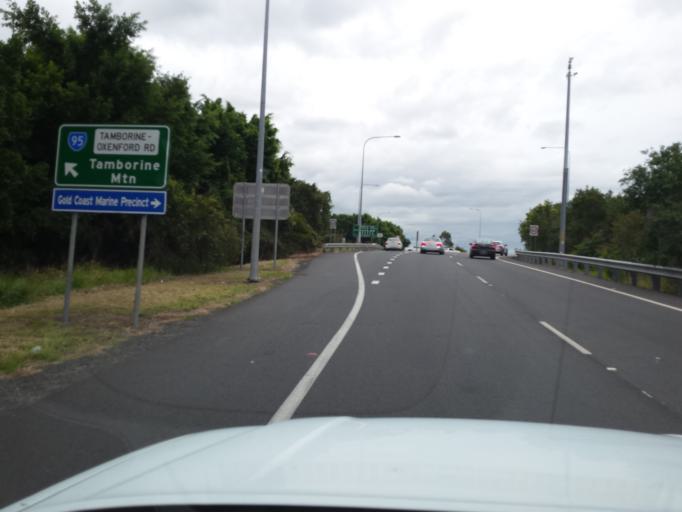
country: AU
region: Queensland
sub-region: Gold Coast
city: Oxenford
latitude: -27.8866
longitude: 153.3149
